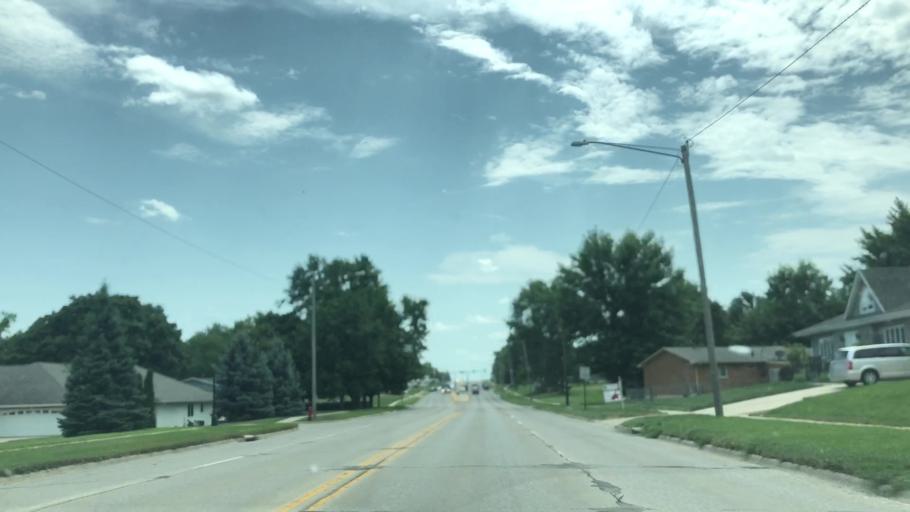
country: US
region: Iowa
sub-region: Marshall County
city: Marshalltown
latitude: 42.0309
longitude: -92.9127
